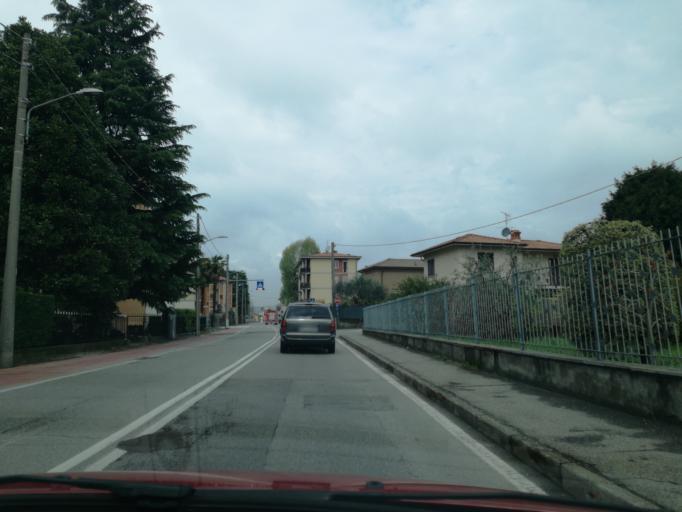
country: IT
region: Lombardy
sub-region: Provincia di Lecco
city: Merate
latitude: 45.6958
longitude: 9.4118
